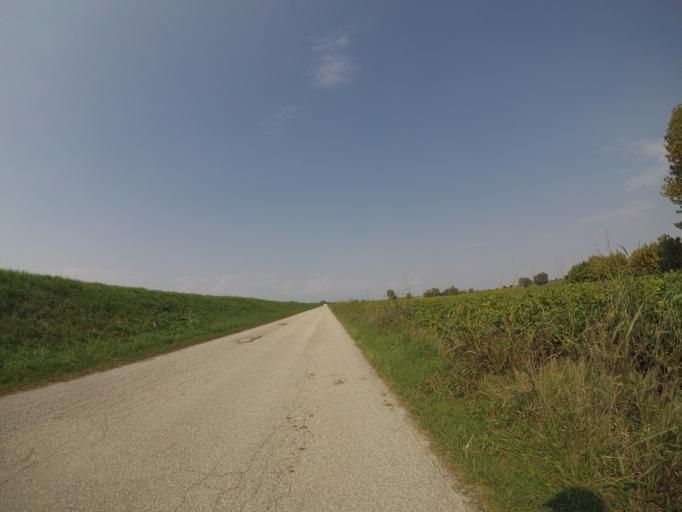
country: IT
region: Friuli Venezia Giulia
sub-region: Provincia di Udine
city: Camino al Tagliamento
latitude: 45.9311
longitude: 12.9221
